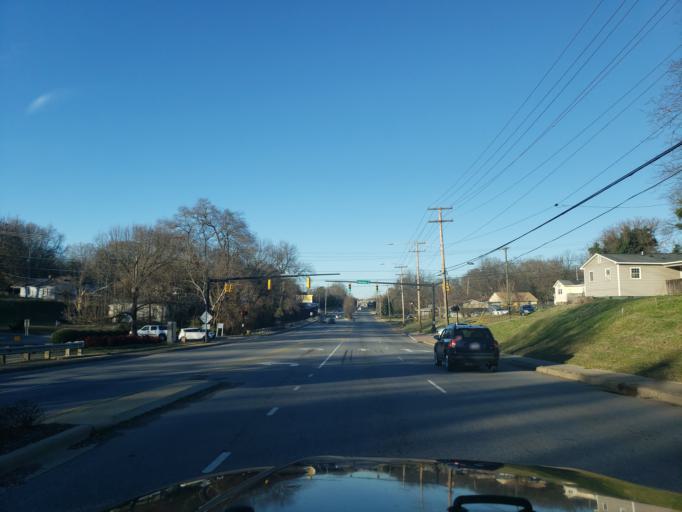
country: US
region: North Carolina
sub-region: Gaston County
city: Gastonia
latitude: 35.2724
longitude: -81.1877
